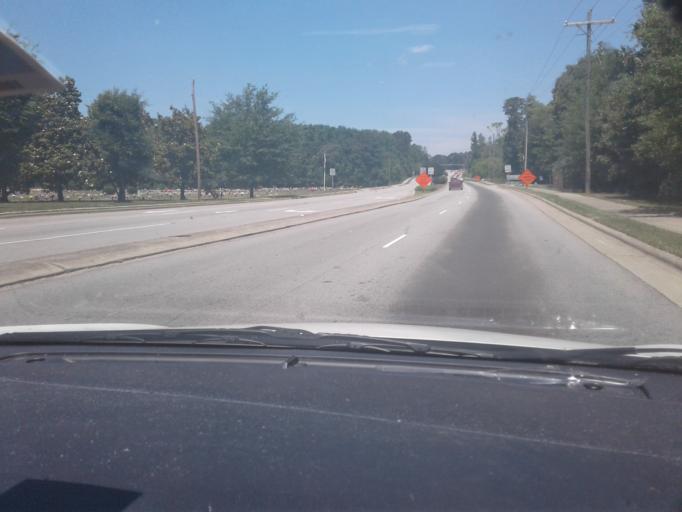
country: US
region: North Carolina
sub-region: Wake County
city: Fuquay-Varina
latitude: 35.6055
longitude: -78.8047
